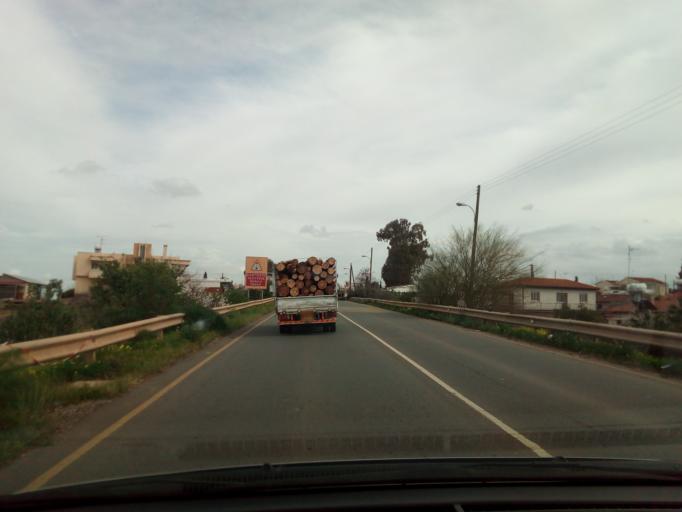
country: CY
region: Lefkosia
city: Peristerona
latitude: 35.1328
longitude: 33.0848
